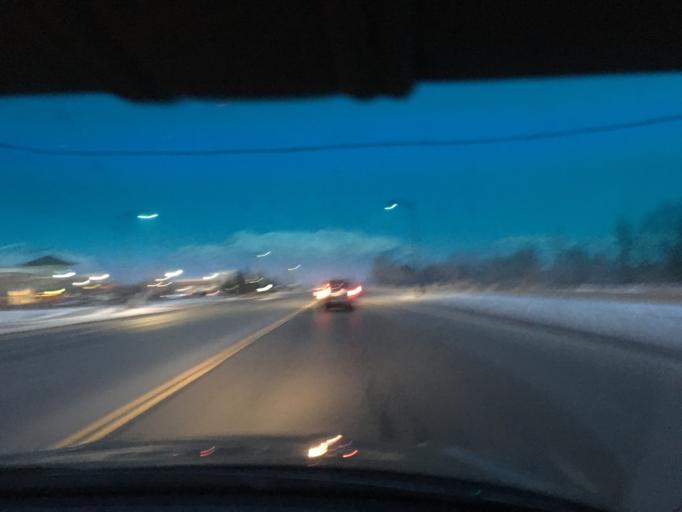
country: US
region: Utah
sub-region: Utah County
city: Saratoga Springs
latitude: 40.3874
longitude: -111.9126
